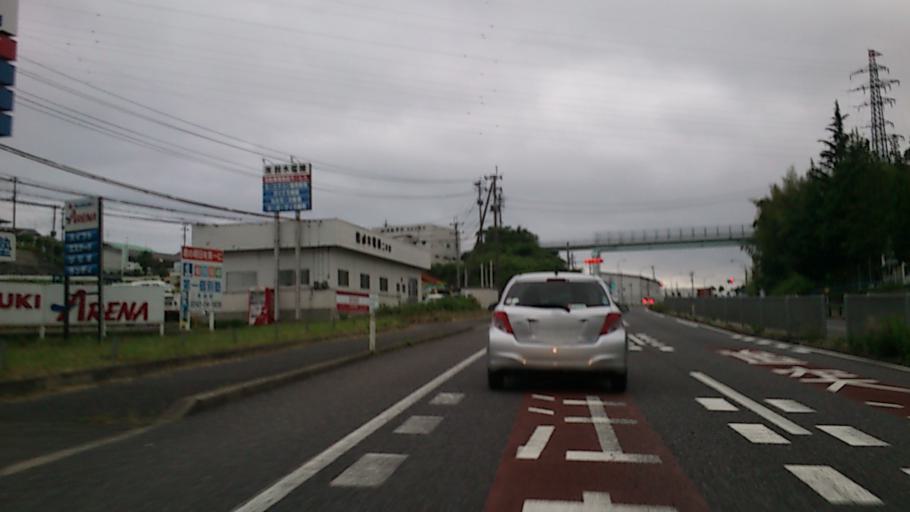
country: JP
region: Fukushima
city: Nihommatsu
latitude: 37.5747
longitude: 140.4206
